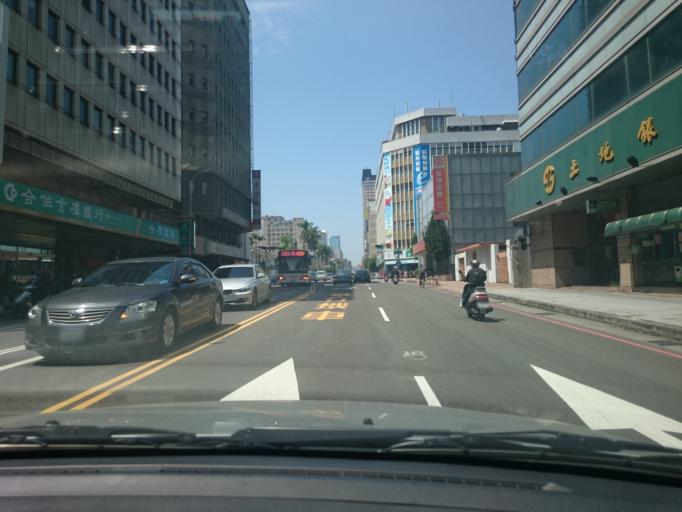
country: TW
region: Taiwan
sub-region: Taichung City
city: Taichung
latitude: 24.1381
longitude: 120.6798
